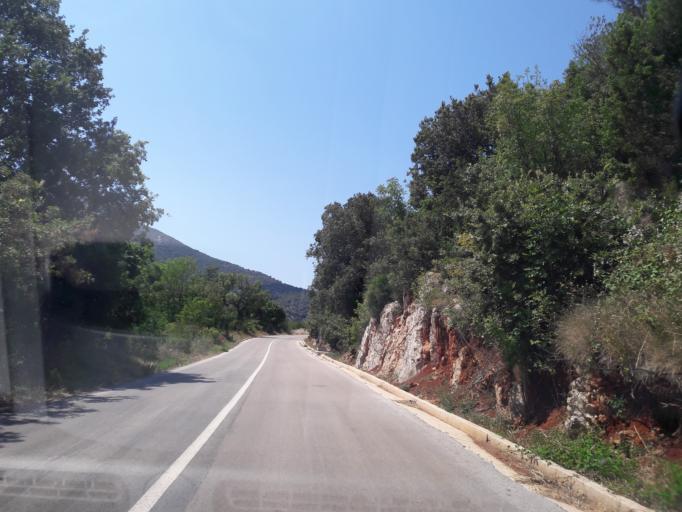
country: HR
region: Dubrovacko-Neretvanska
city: Orebic
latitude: 43.0097
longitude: 17.2111
